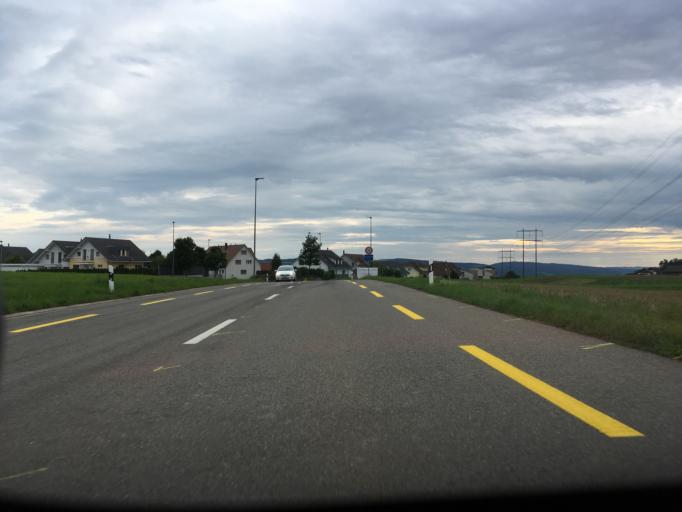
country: CH
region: Zurich
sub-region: Bezirk Uster
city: Gutenswil
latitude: 47.3888
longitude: 8.7228
